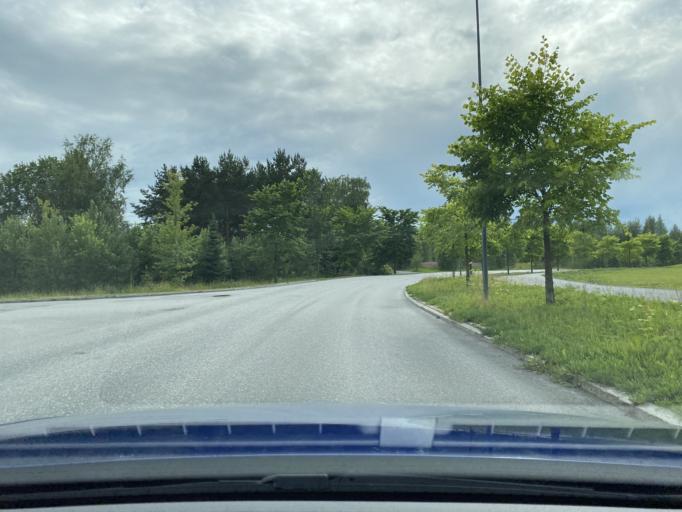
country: FI
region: Pirkanmaa
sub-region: Tampere
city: Lempaeaelae
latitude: 61.3567
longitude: 23.7956
